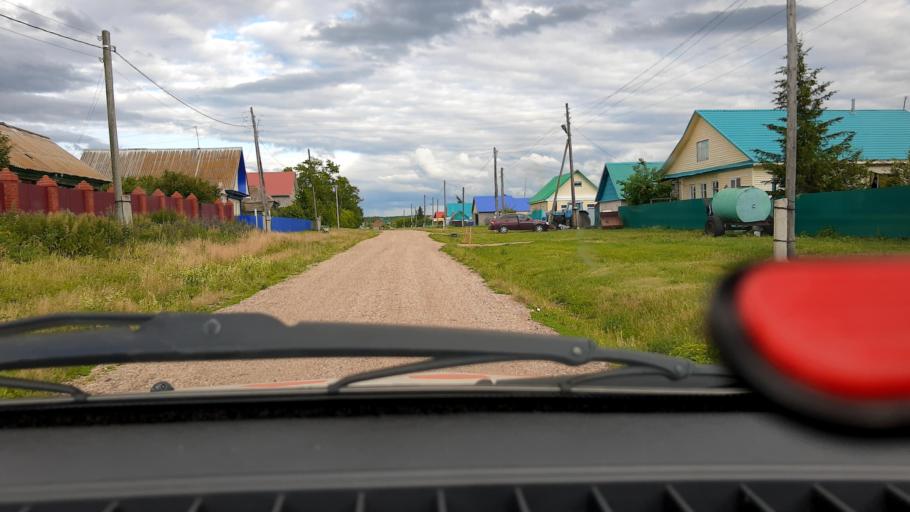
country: RU
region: Bashkortostan
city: Karmaskaly
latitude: 54.4195
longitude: 56.0258
